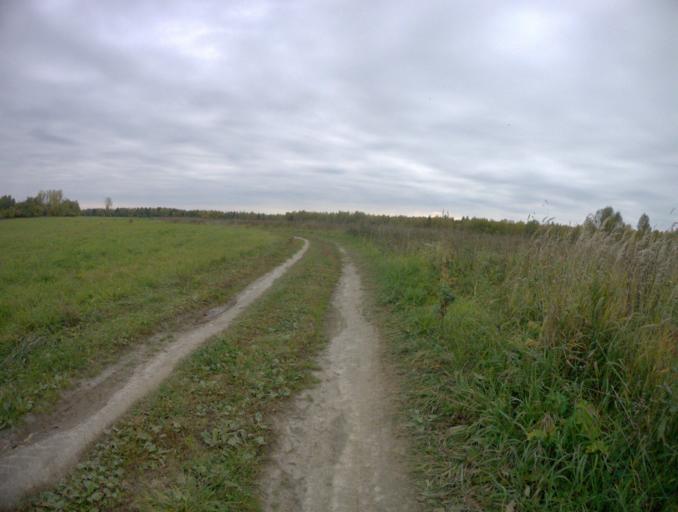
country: RU
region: Vladimir
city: Mstera
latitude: 56.3677
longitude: 41.8631
